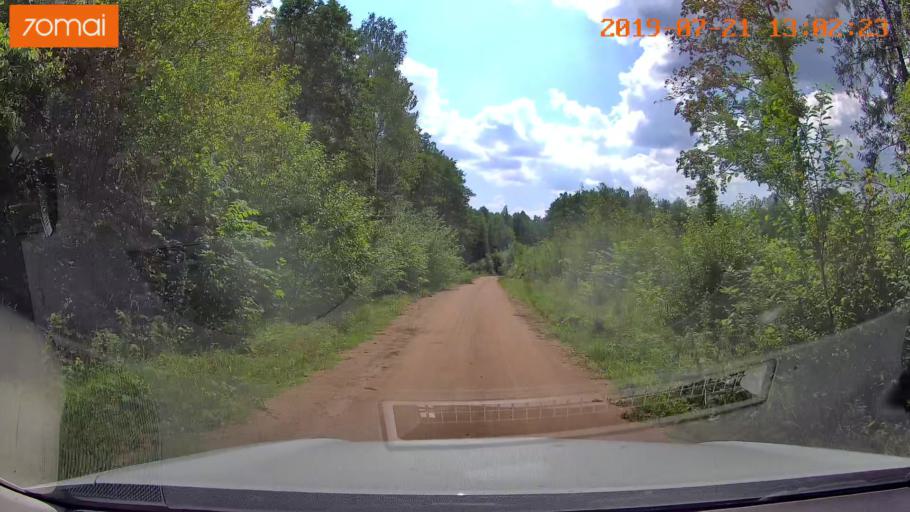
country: BY
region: Grodnenskaya
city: Lyubcha
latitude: 53.8478
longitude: 26.0246
